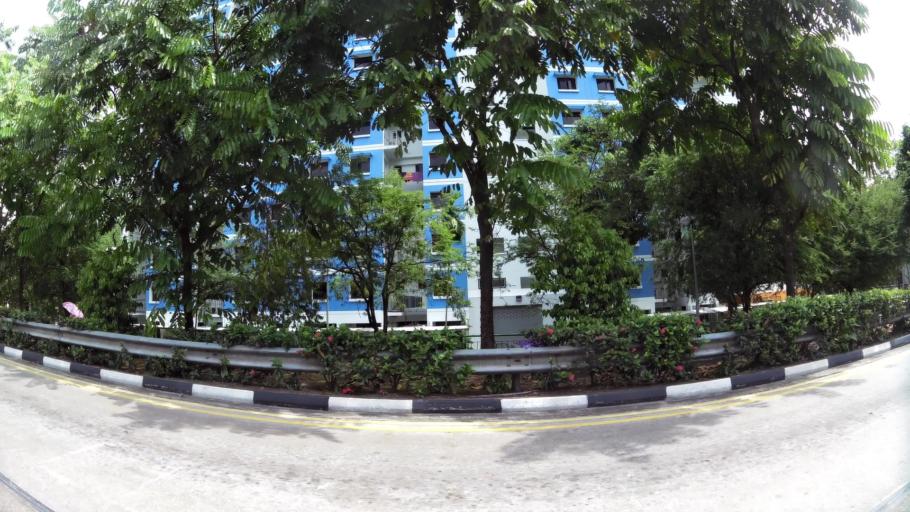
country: MY
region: Johor
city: Johor Bahru
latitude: 1.3380
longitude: 103.6959
